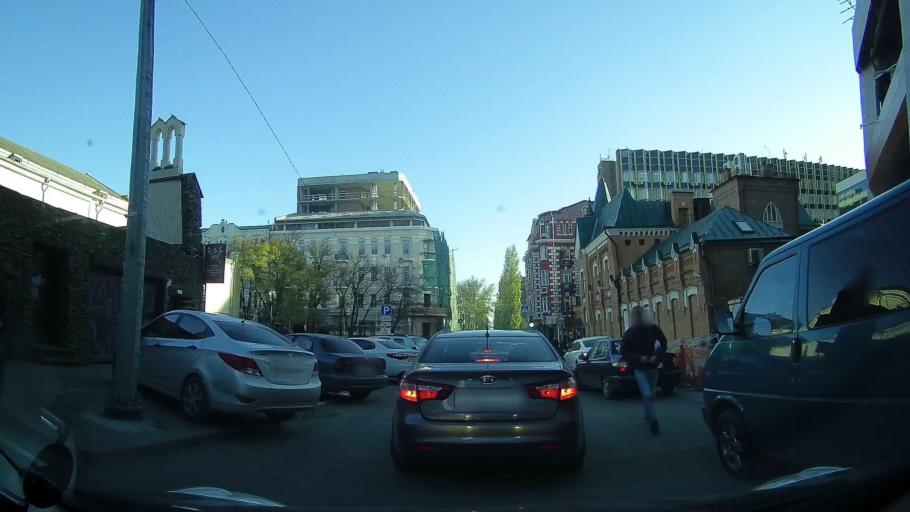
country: RU
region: Rostov
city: Rostov-na-Donu
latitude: 47.2266
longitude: 39.7363
